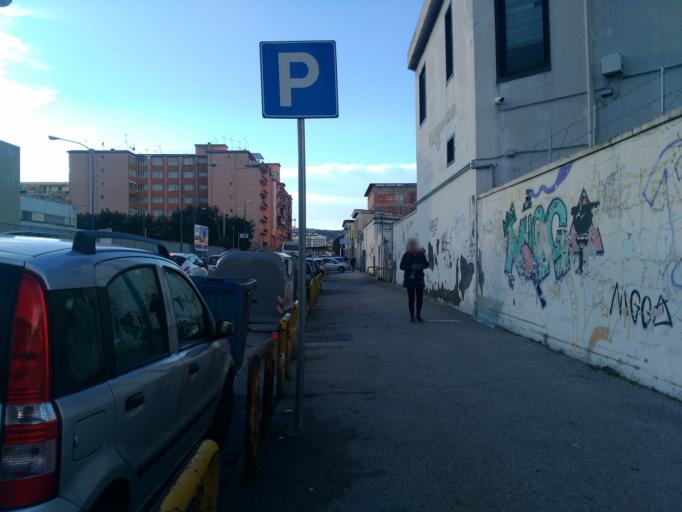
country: IT
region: Campania
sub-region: Provincia di Napoli
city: Napoli
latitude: 40.8494
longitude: 14.2812
